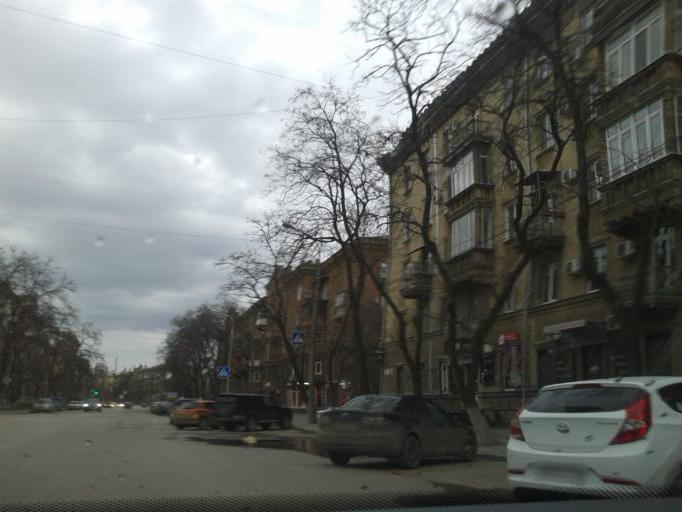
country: RU
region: Volgograd
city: Volgograd
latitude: 48.7081
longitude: 44.5238
